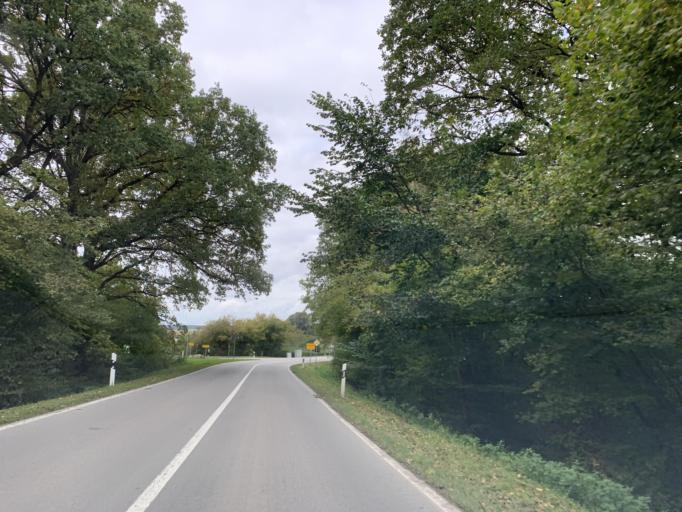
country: DE
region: Mecklenburg-Vorpommern
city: Blankensee
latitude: 53.4024
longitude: 13.2645
